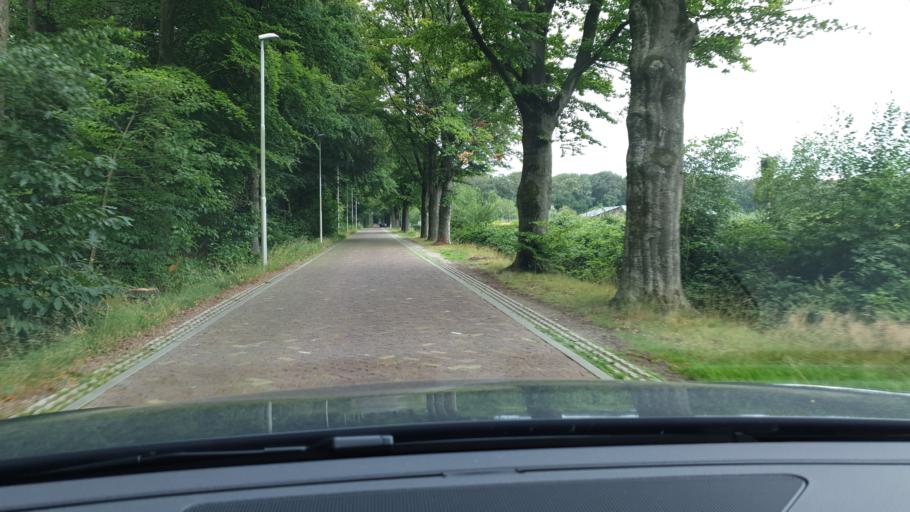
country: NL
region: North Brabant
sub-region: Gemeente Eindhoven
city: Meerhoven
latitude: 51.4647
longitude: 5.4306
